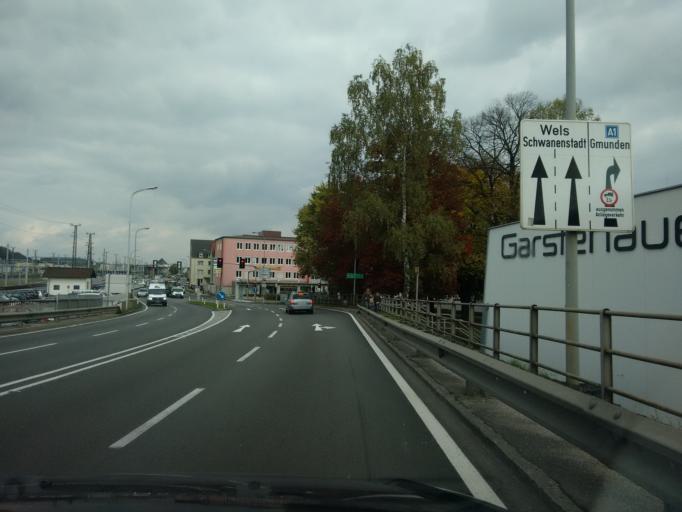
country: AT
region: Upper Austria
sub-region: Politischer Bezirk Vocklabruck
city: Attnang-Puchheim
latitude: 48.0084
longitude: 13.7176
